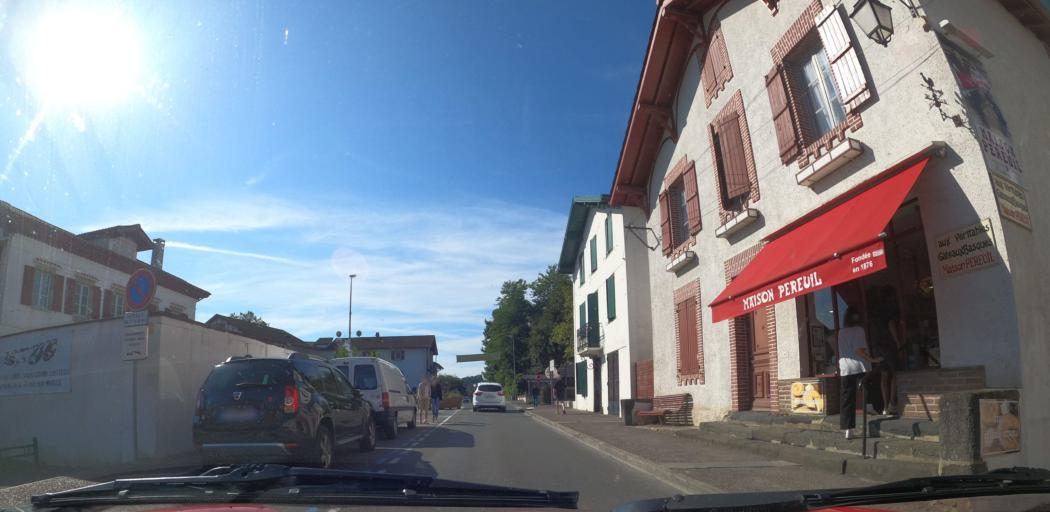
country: FR
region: Aquitaine
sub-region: Departement des Pyrenees-Atlantiques
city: Saint-Pee-sur-Nivelle
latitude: 43.3547
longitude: -1.5504
